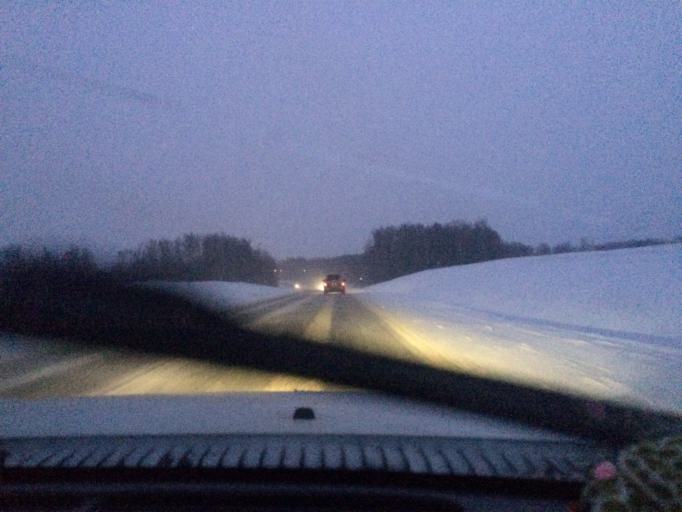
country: RU
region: Tula
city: Kosaya Gora
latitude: 54.1700
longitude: 37.4592
